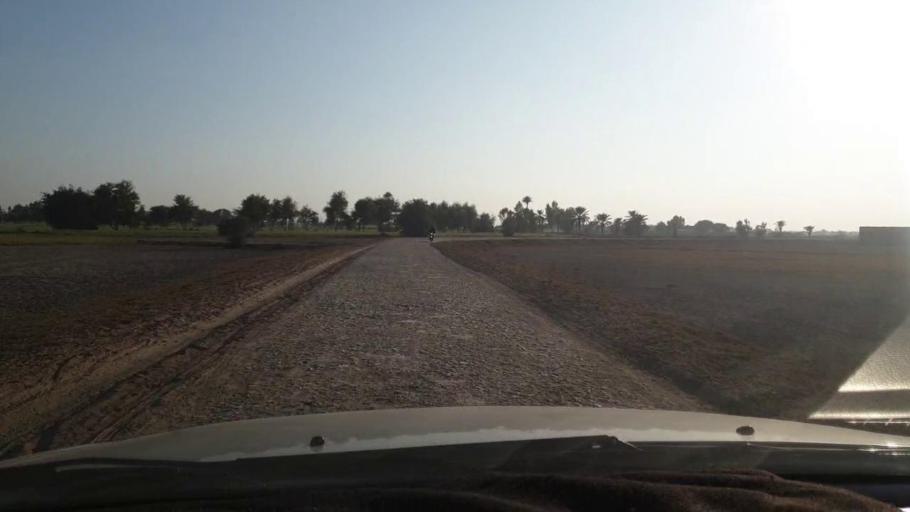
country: PK
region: Sindh
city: Mirpur Mathelo
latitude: 28.0076
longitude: 69.5348
